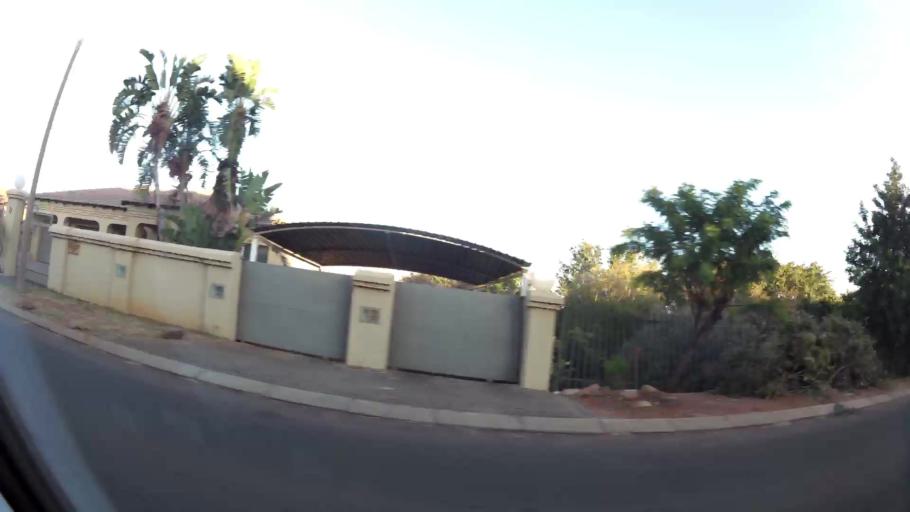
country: ZA
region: North-West
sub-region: Bojanala Platinum District Municipality
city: Rustenburg
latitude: -25.7080
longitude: 27.2335
